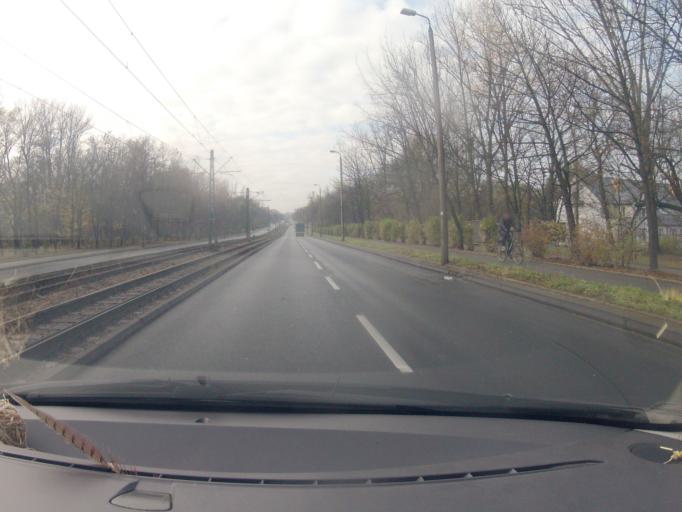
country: PL
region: Lesser Poland Voivodeship
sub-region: Powiat wielicki
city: Kokotow
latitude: 50.0780
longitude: 20.0591
